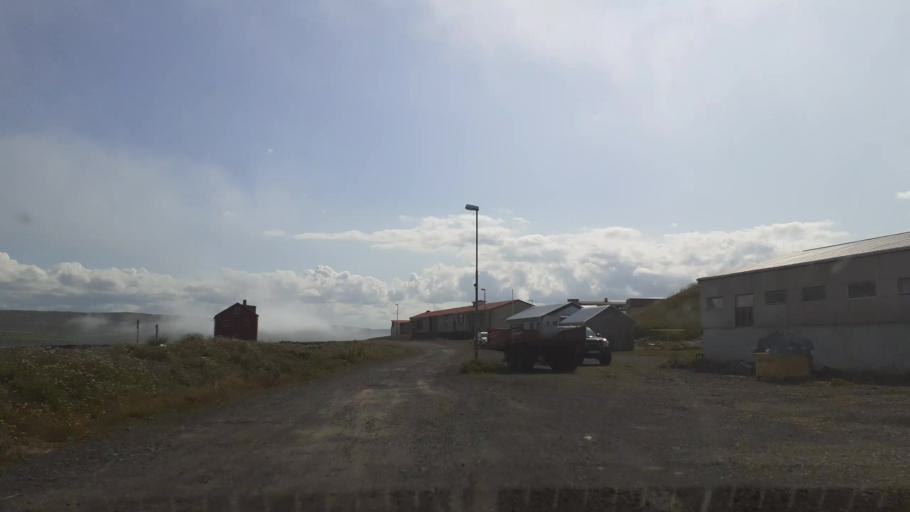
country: IS
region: West
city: Borgarnes
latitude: 65.2107
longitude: -21.0954
